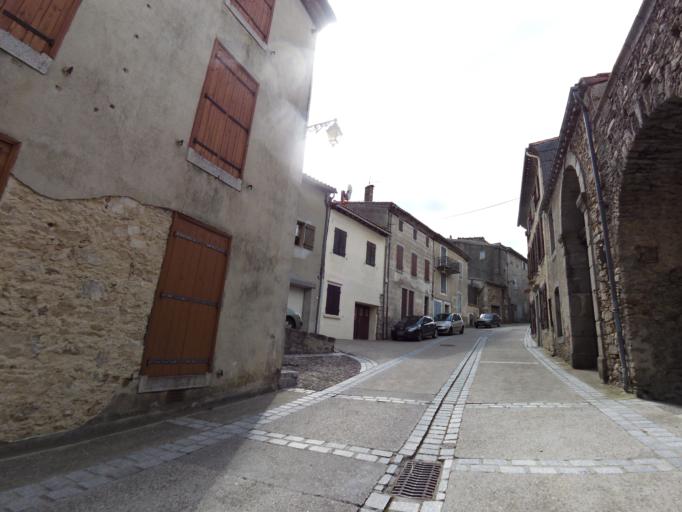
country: FR
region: Languedoc-Roussillon
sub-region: Departement de l'Aude
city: Alzonne
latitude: 43.3604
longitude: 2.1684
